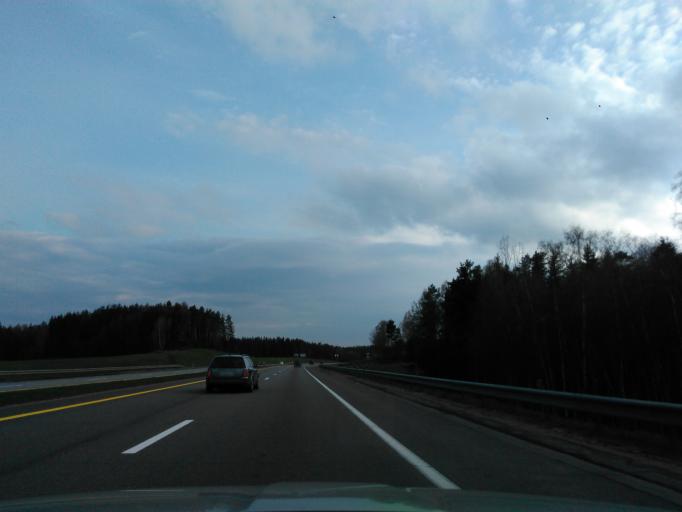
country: BY
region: Minsk
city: Astrashytski Haradok
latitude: 54.0486
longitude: 27.7018
